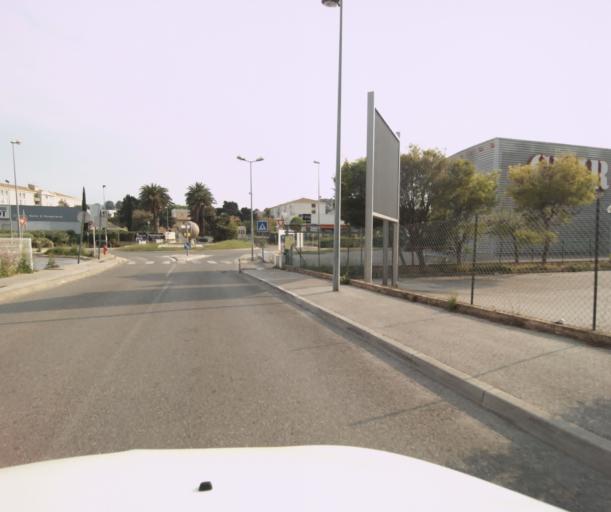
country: FR
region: Provence-Alpes-Cote d'Azur
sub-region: Departement du Var
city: La Garde
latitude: 43.1381
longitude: 6.0088
